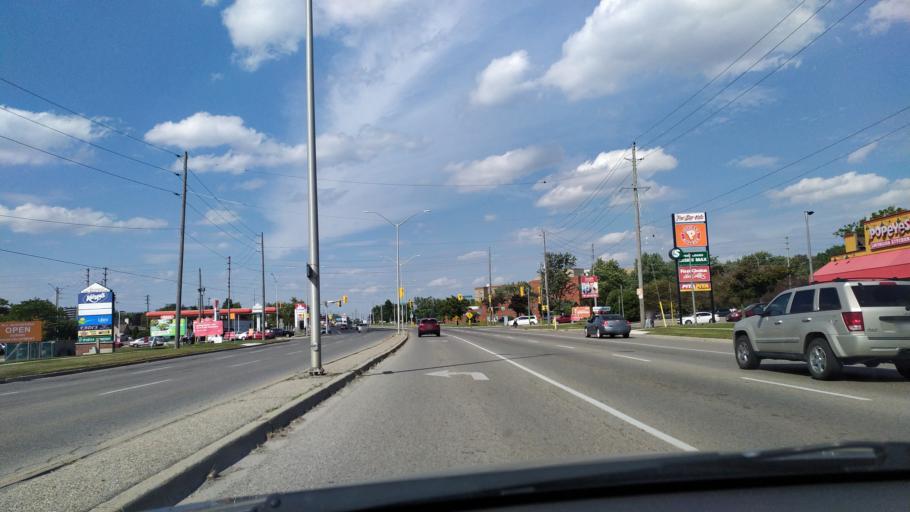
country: CA
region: Ontario
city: London
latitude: 42.9425
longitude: -81.2255
